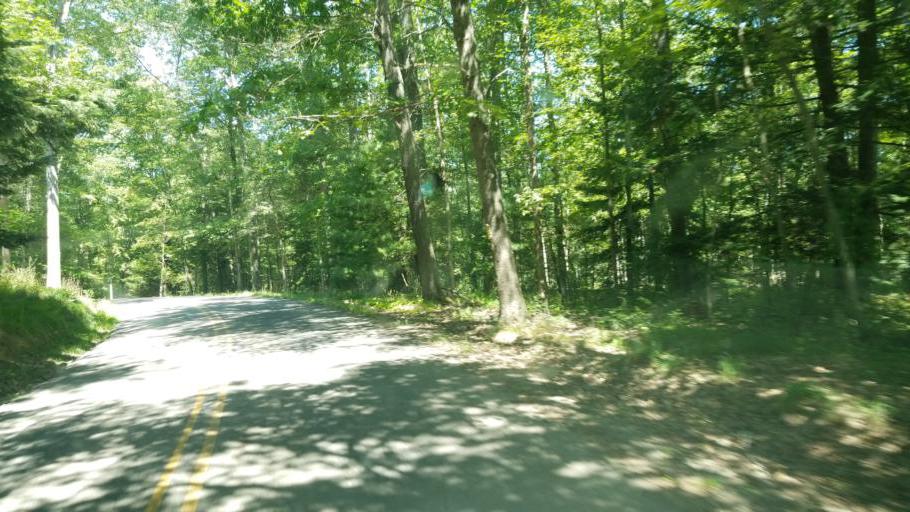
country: US
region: Pennsylvania
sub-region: Clarion County
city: Knox
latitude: 41.1844
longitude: -79.4852
